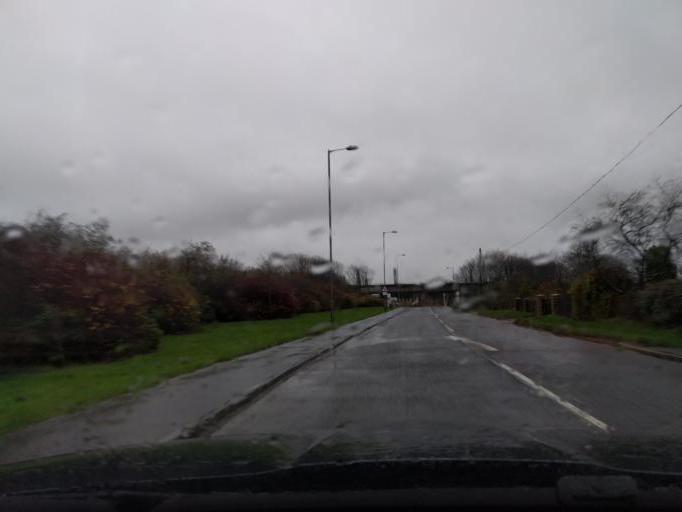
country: GB
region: England
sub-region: Northumberland
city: Newbiggin-by-the-Sea
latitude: 55.1917
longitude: -1.5247
